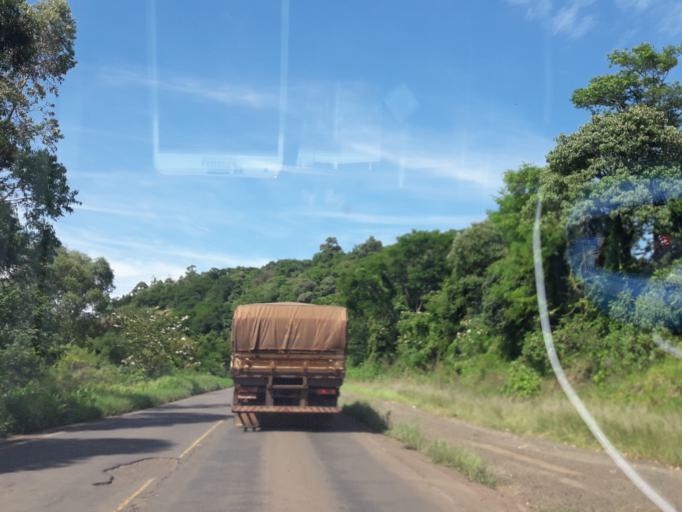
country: AR
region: Misiones
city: Bernardo de Irigoyen
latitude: -26.4858
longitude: -53.5036
